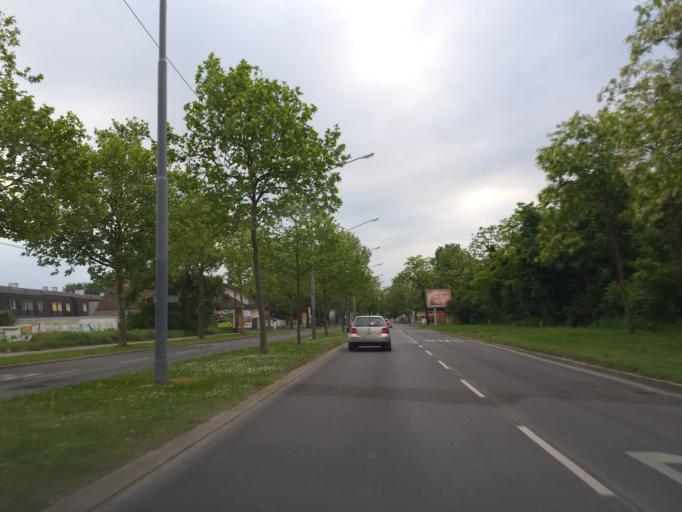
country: AT
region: Lower Austria
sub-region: Politischer Bezirk Ganserndorf
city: Gross-Enzersdorf
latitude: 48.2166
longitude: 16.4975
